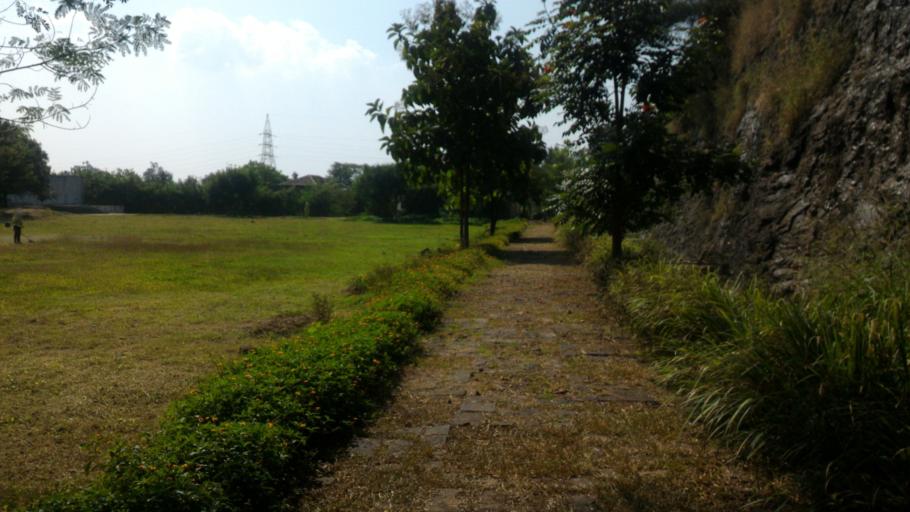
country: IN
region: Karnataka
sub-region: Belgaum
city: Belgaum
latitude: 15.8234
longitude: 74.4799
